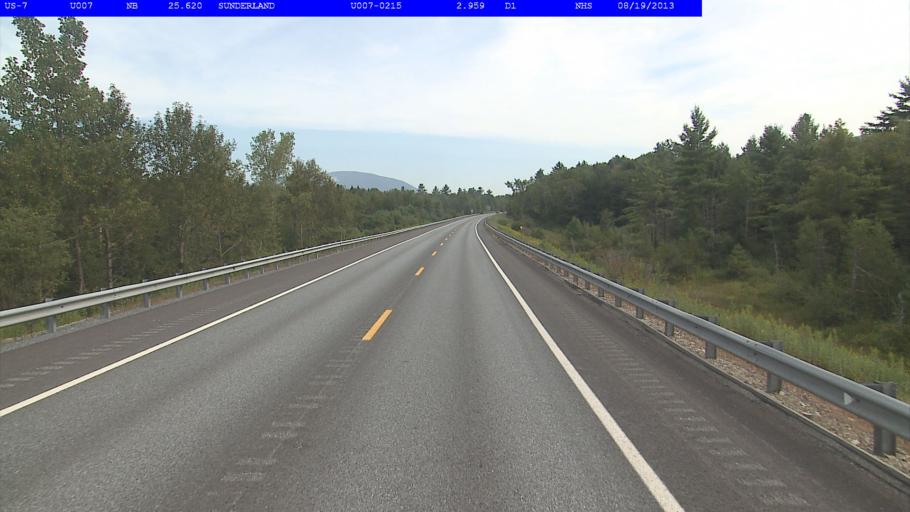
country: US
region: Vermont
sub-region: Bennington County
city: Arlington
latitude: 43.0668
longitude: -73.1235
